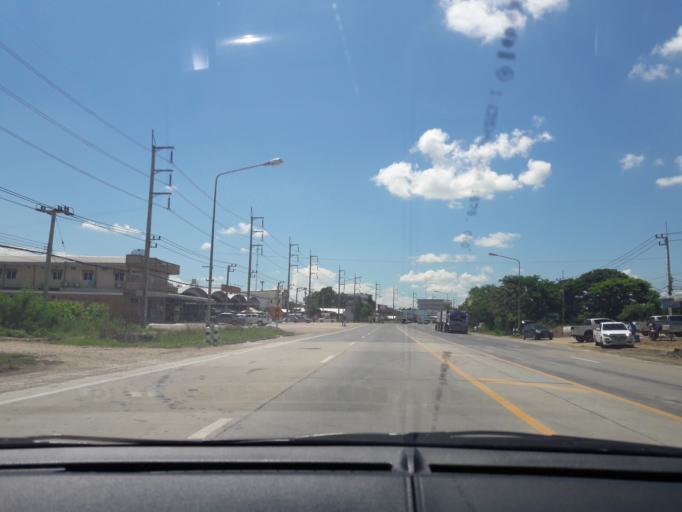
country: TH
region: Kanchanaburi
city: Tha Maka
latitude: 14.0365
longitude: 99.7963
